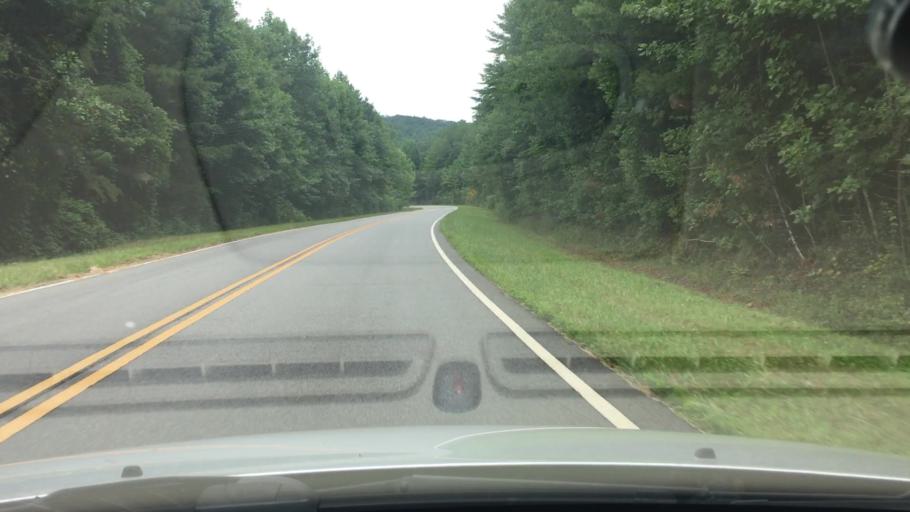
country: US
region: Georgia
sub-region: Lumpkin County
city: Dahlonega
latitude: 34.6235
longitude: -83.8977
